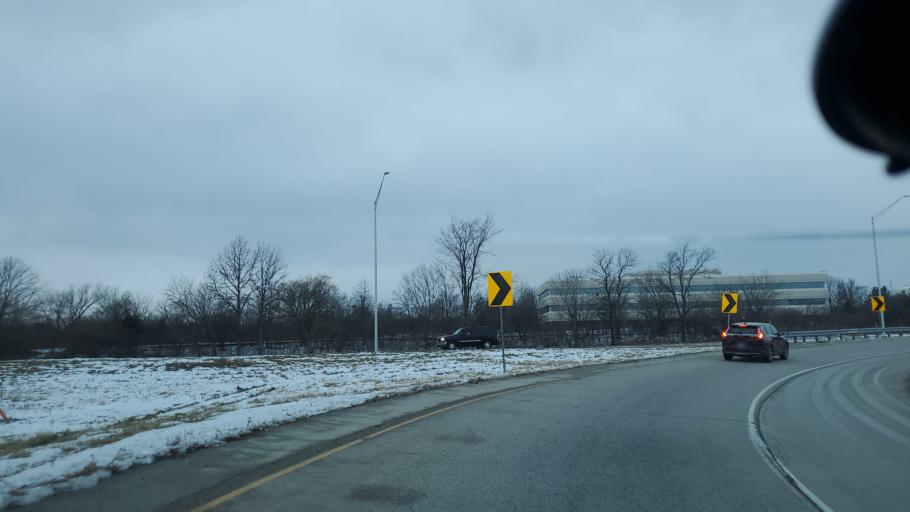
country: US
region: Illinois
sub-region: Kane County
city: North Aurora
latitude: 41.7987
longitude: -88.2836
